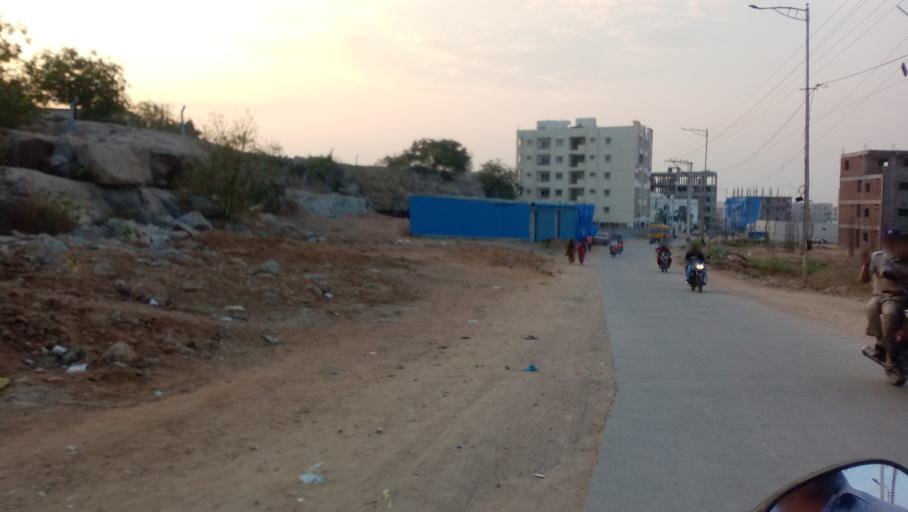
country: IN
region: Telangana
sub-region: Medak
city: Serilingampalle
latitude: 17.5210
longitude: 78.3035
